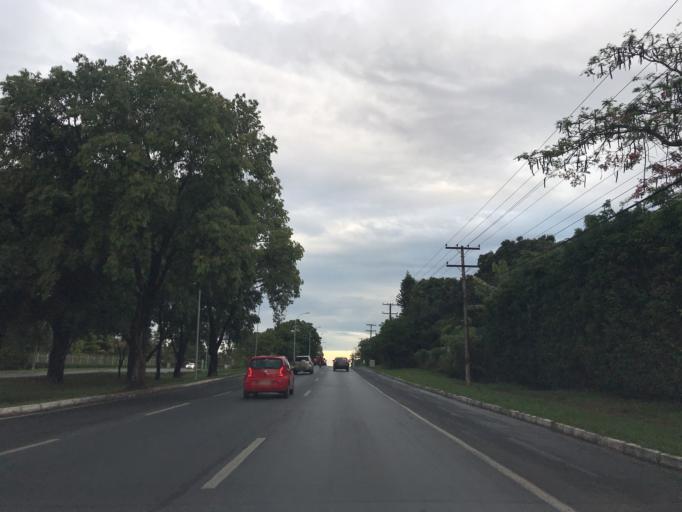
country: BR
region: Federal District
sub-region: Brasilia
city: Brasilia
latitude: -15.8590
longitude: -47.8670
